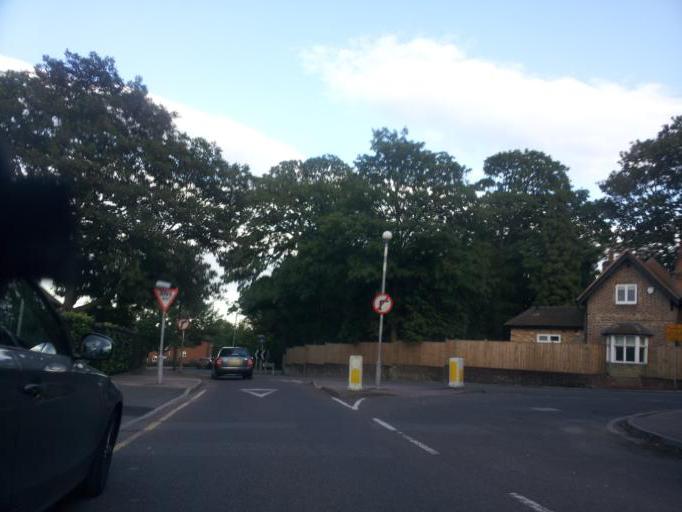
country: GB
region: England
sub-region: Greater London
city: Bromley
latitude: 51.4078
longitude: -0.0041
